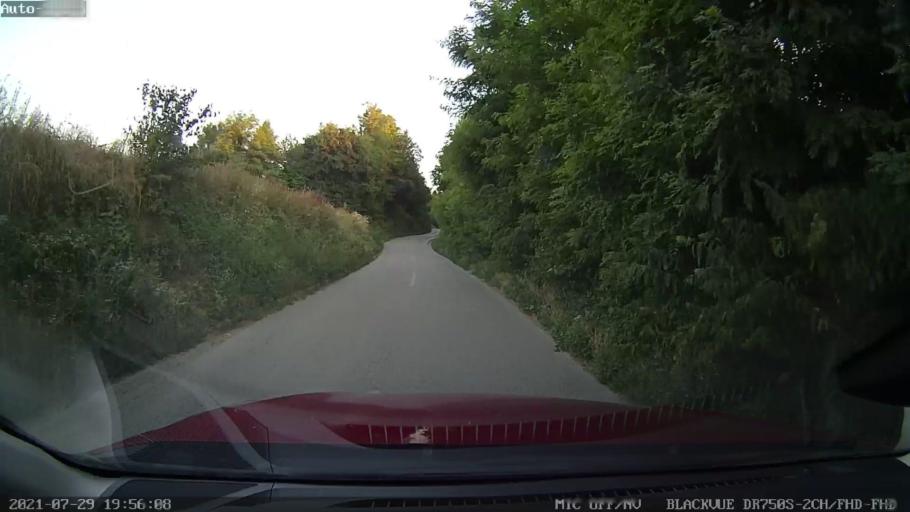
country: HR
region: Varazdinska
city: Jalzabet
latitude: 46.2512
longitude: 16.4720
